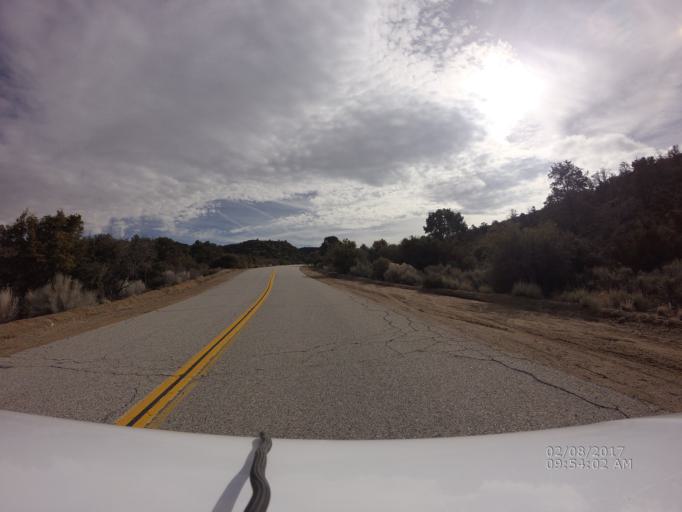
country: US
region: California
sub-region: San Bernardino County
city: Pinon Hills
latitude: 34.4219
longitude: -117.7993
